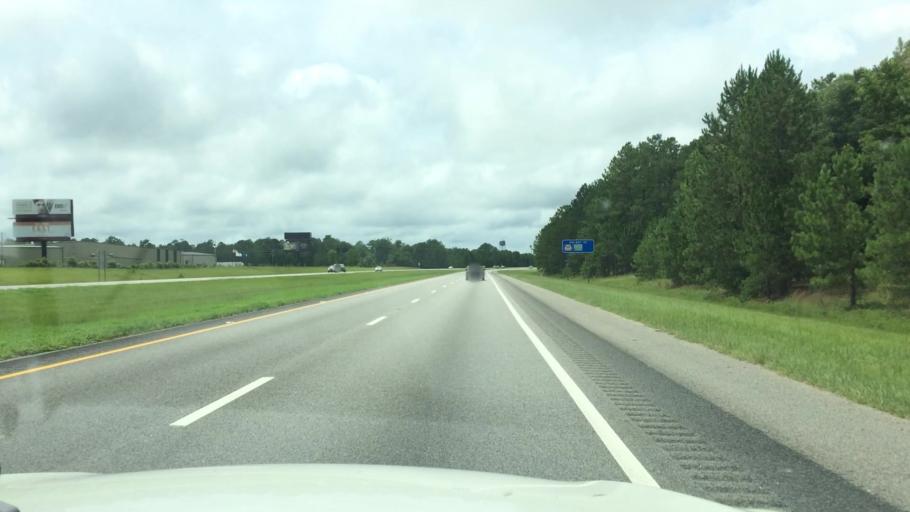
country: US
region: South Carolina
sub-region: Florence County
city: Timmonsville
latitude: 34.2027
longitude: -79.8989
